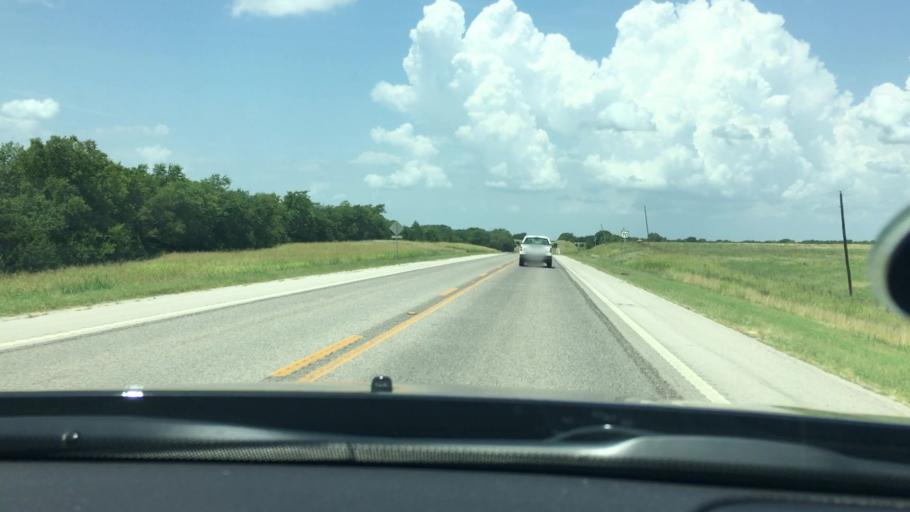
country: US
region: Oklahoma
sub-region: Marshall County
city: Oakland
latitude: 34.1000
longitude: -96.8892
